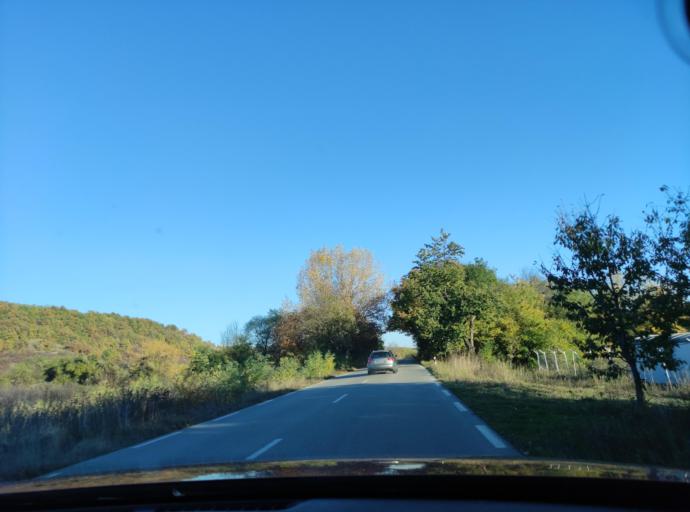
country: BG
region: Montana
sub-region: Obshtina Chiprovtsi
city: Chiprovtsi
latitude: 43.4283
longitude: 23.0011
